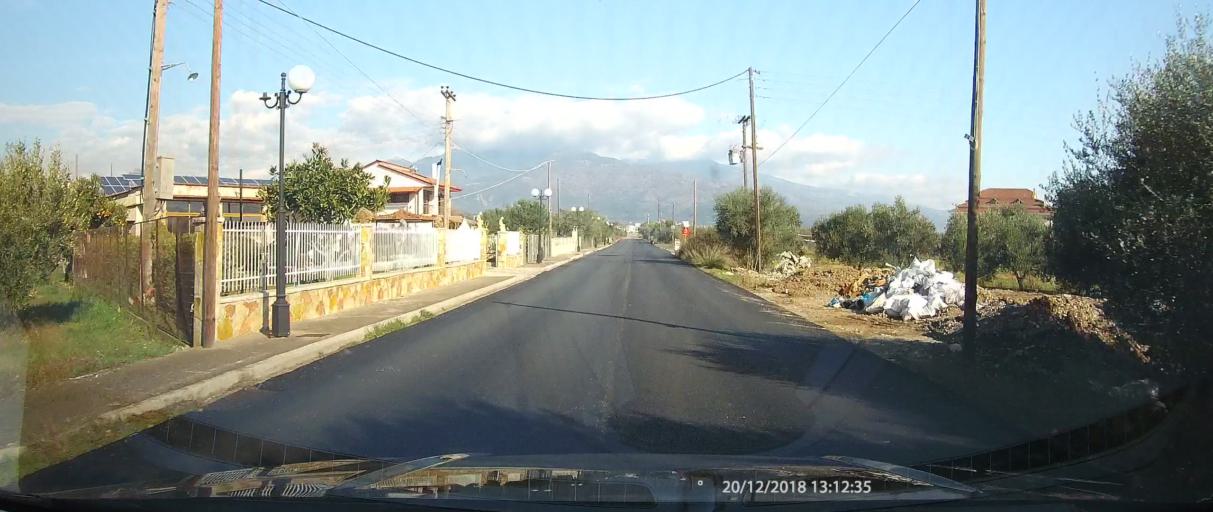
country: GR
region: West Greece
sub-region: Nomos Aitolias kai Akarnanias
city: Kainouryion
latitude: 38.5987
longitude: 21.4714
